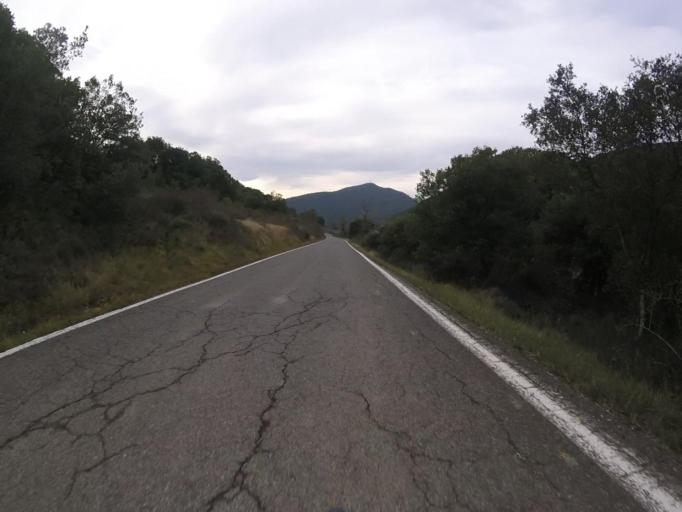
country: ES
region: Navarre
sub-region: Provincia de Navarra
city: Estella
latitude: 42.7077
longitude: -2.0505
